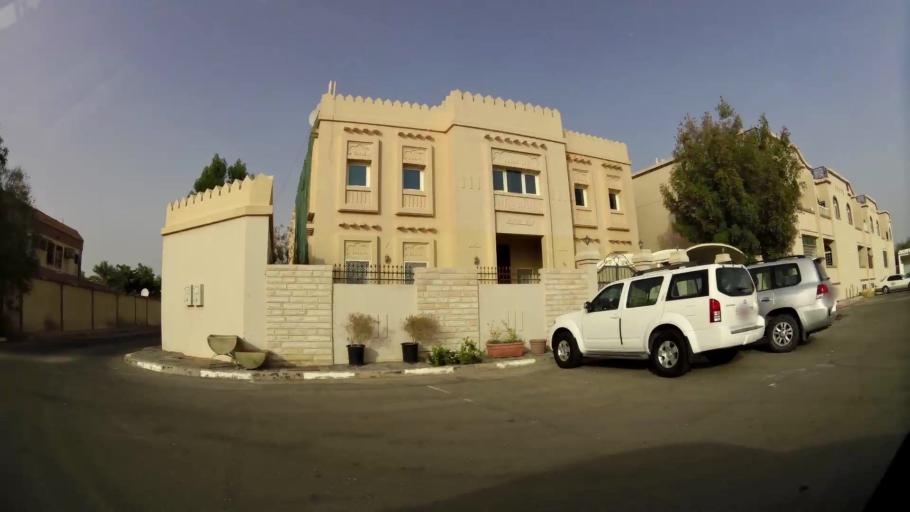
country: AE
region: Abu Dhabi
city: Al Ain
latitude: 24.2208
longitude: 55.7119
